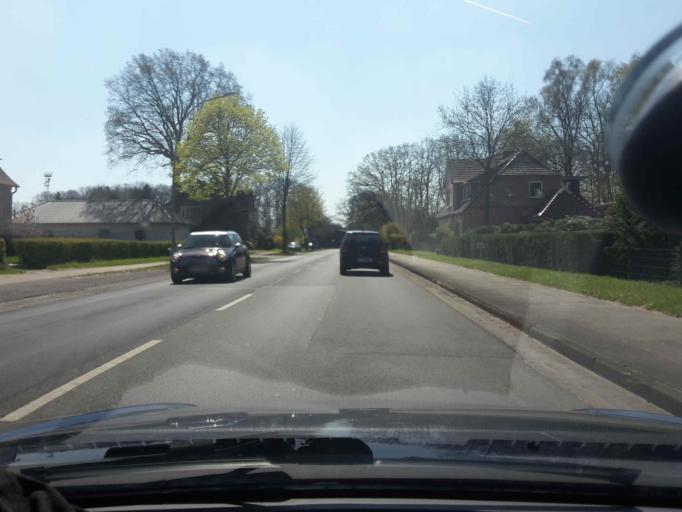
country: DE
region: Lower Saxony
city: Schneverdingen
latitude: 53.0753
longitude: 9.8633
